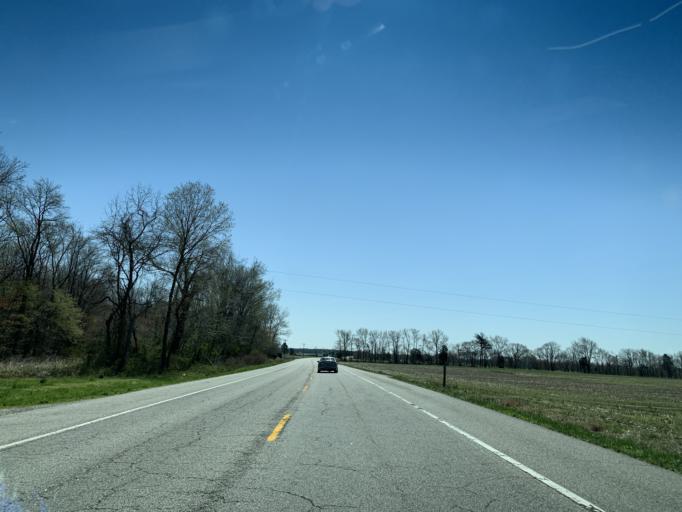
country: US
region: Maryland
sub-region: Queen Anne's County
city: Centreville
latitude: 38.9667
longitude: -75.9969
